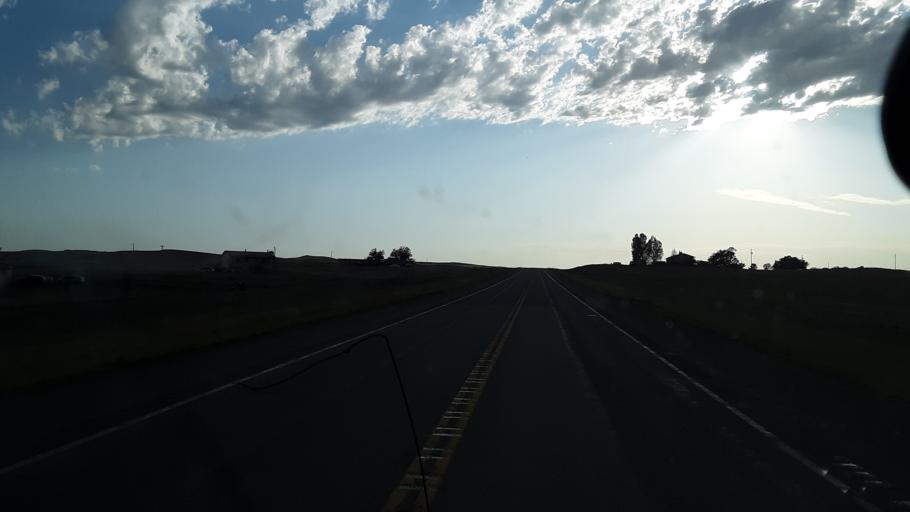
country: US
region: Montana
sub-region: Rosebud County
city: Lame Deer
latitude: 45.5281
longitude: -106.9735
